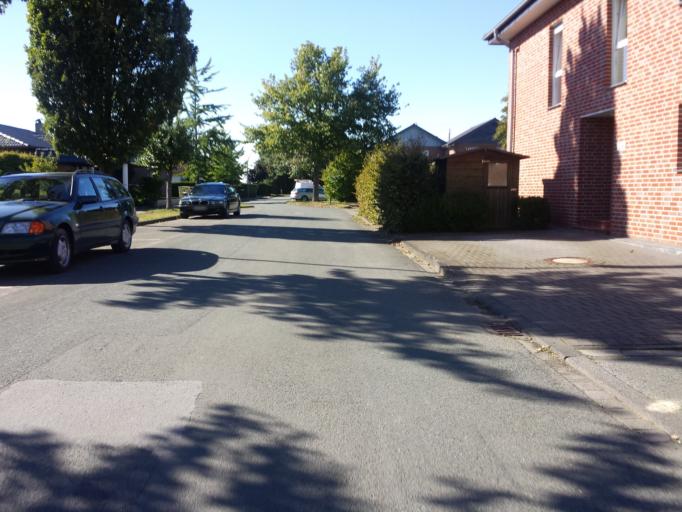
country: DE
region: North Rhine-Westphalia
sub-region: Regierungsbezirk Detmold
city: Langenberg
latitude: 51.7646
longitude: 8.3119
